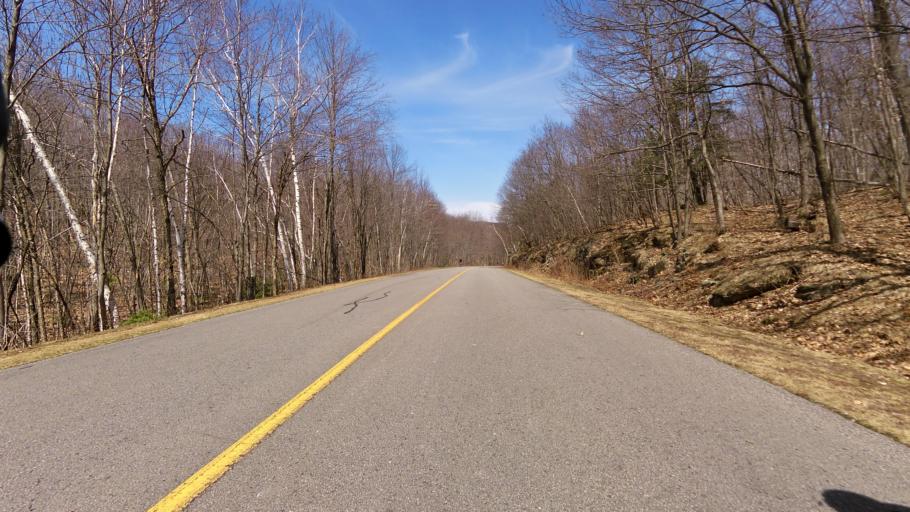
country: CA
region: Quebec
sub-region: Outaouais
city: Gatineau
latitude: 45.4743
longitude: -75.8445
